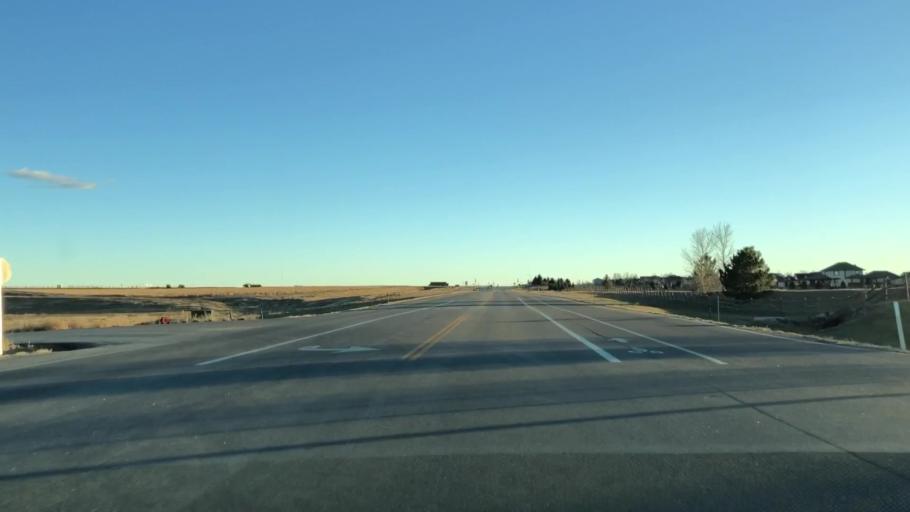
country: US
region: Colorado
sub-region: Weld County
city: Windsor
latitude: 40.4505
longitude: -104.9442
